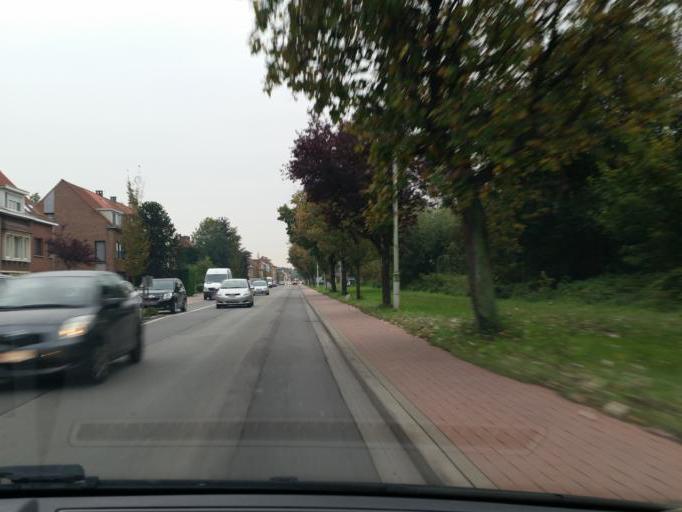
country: BE
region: Flanders
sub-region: Provincie Antwerpen
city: Hemiksem
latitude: 51.1533
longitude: 4.3420
